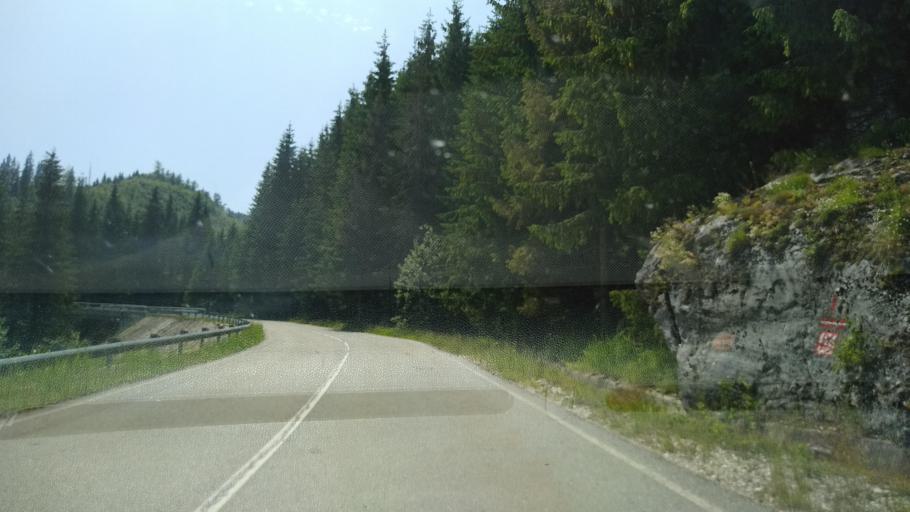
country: RO
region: Gorj
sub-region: Comuna Pades
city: Closani
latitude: 45.2637
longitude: 22.8719
